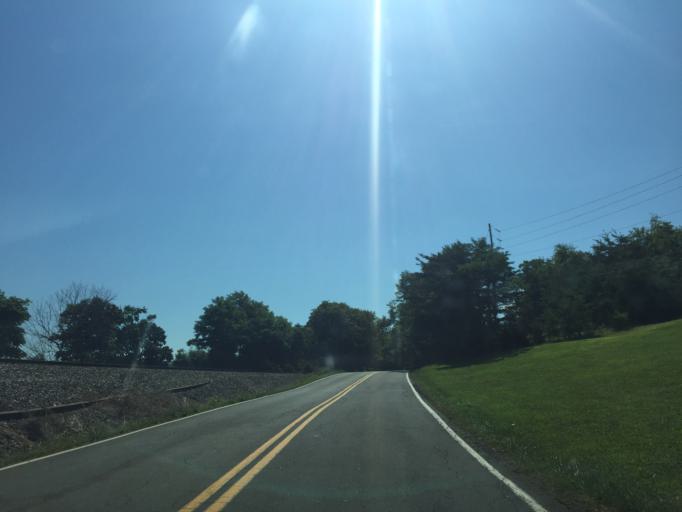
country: US
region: Virginia
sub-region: Warren County
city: Front Royal
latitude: 38.9296
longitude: -78.1610
